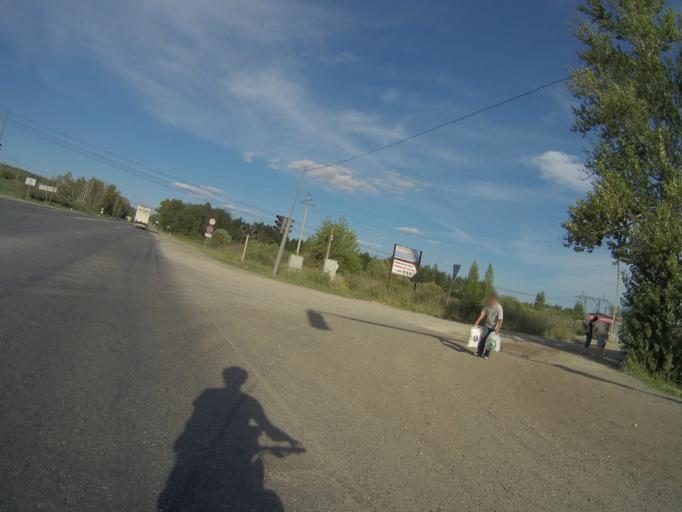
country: RU
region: Vladimir
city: Raduzhnyy
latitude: 56.0890
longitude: 40.2289
